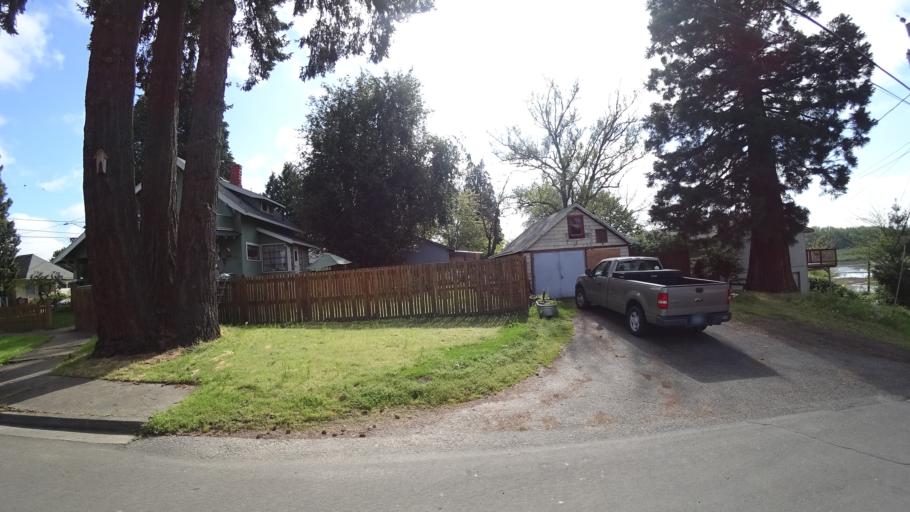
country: US
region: Oregon
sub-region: Washington County
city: Hillsboro
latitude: 45.5147
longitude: -122.9864
